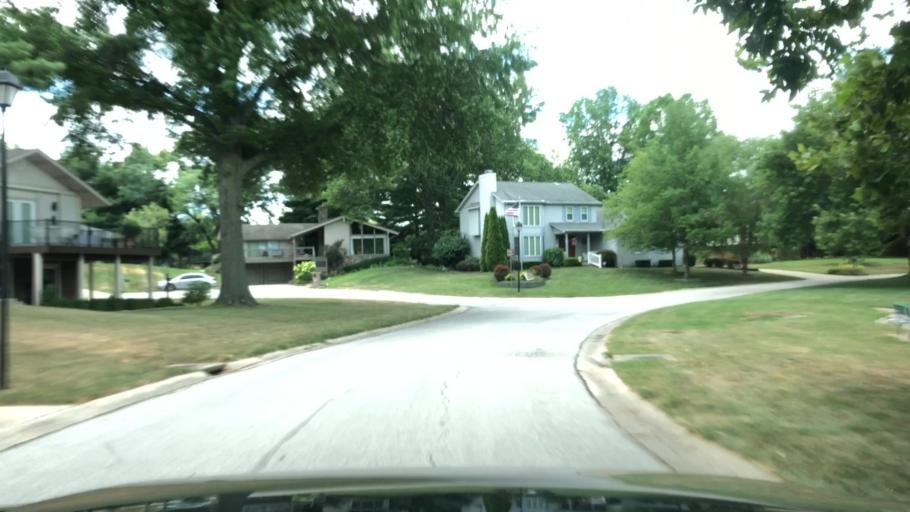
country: US
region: Missouri
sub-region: Saint Charles County
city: Lake Saint Louis
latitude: 38.7981
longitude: -90.7895
